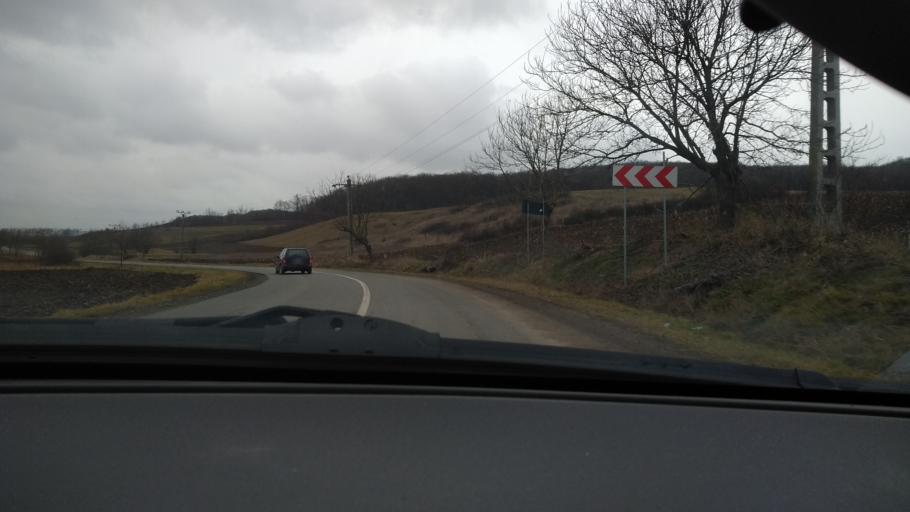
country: RO
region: Mures
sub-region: Comuna Bereni
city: Bereni
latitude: 46.5481
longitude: 24.8419
